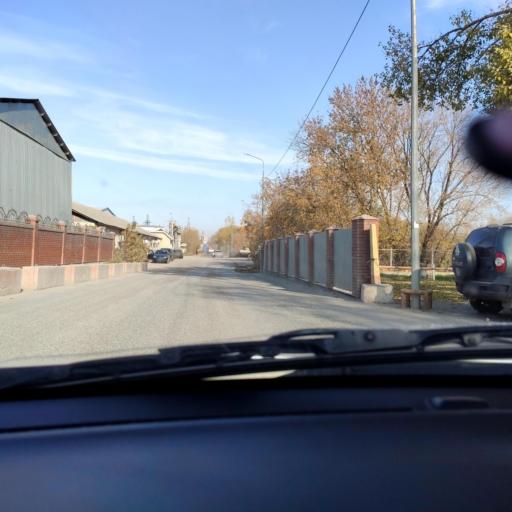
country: RU
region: Tatarstan
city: Verkhniy Uslon
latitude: 55.8016
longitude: 49.0456
